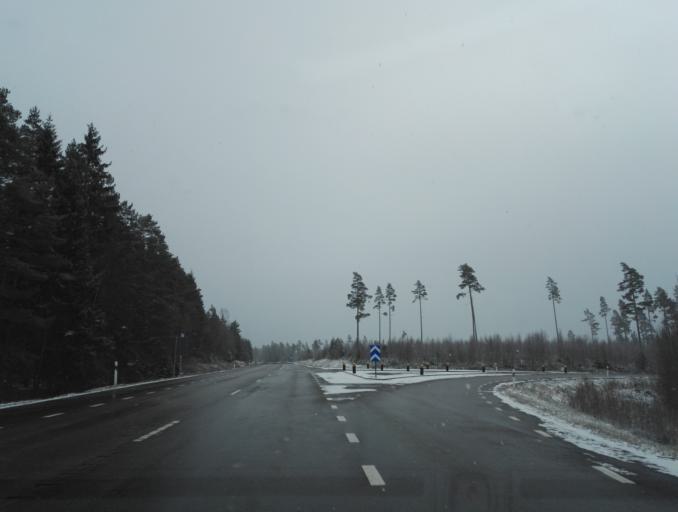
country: SE
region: Kronoberg
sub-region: Uppvidinge Kommun
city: Lenhovda
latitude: 56.9217
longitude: 15.3645
